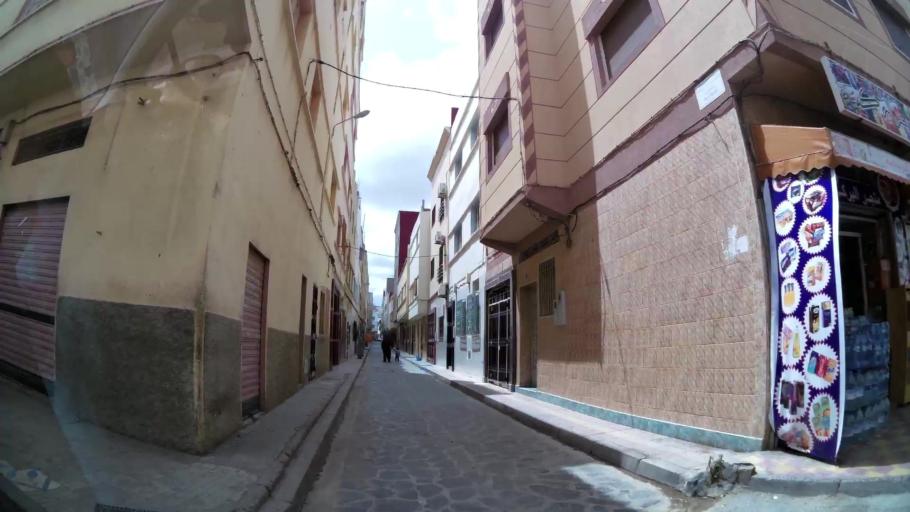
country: MA
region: Oriental
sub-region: Nador
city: Nador
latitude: 35.1735
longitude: -2.9289
